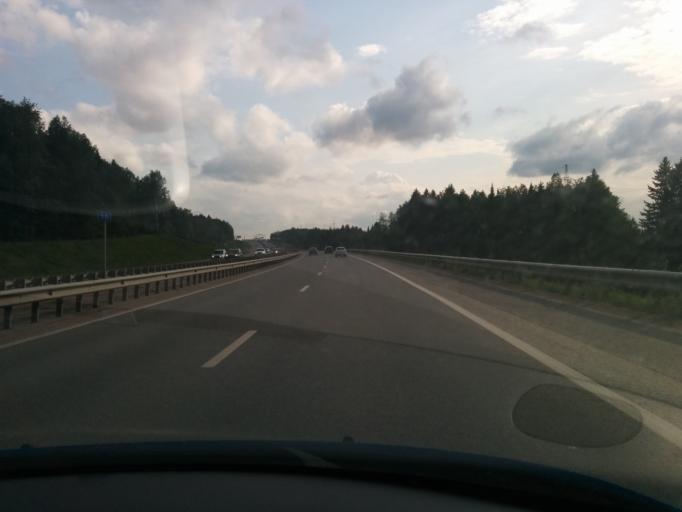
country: RU
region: Perm
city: Ferma
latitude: 58.0127
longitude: 56.4029
